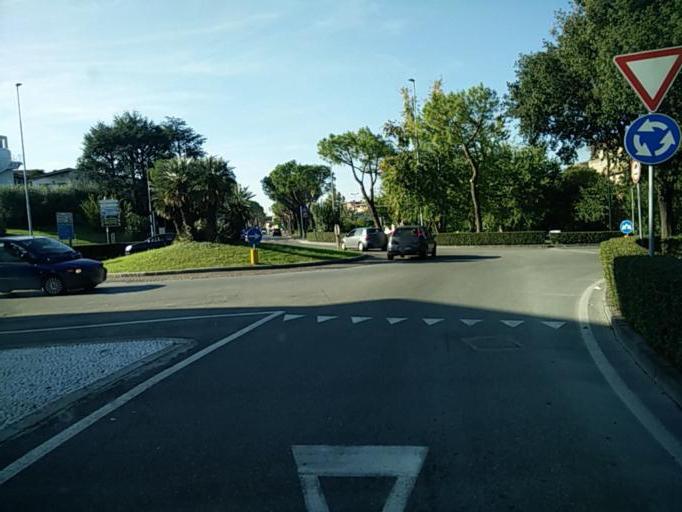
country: IT
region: Lombardy
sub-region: Provincia di Brescia
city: Desenzano del Garda
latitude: 45.4676
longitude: 10.5386
